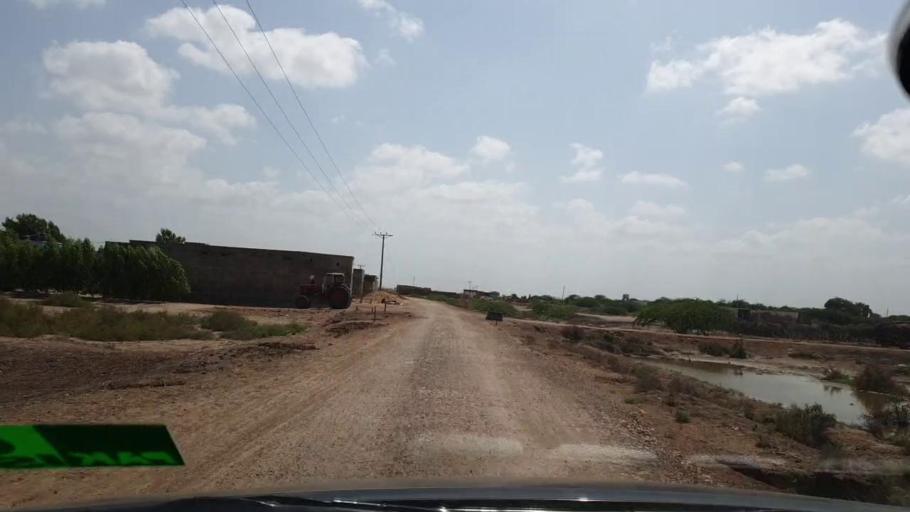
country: PK
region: Sindh
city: Kadhan
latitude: 24.6169
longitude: 69.1855
